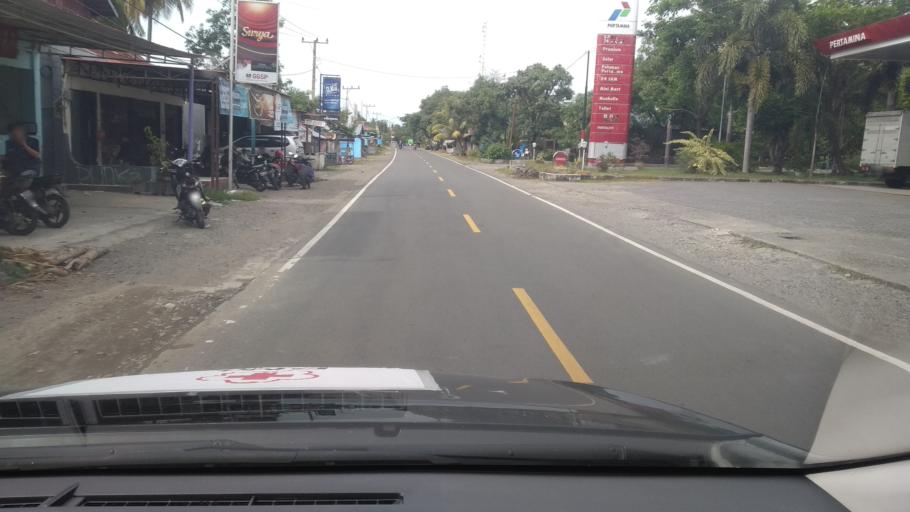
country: ID
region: Sulawesi Barat
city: Malunda
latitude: -3.0070
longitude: 118.8565
